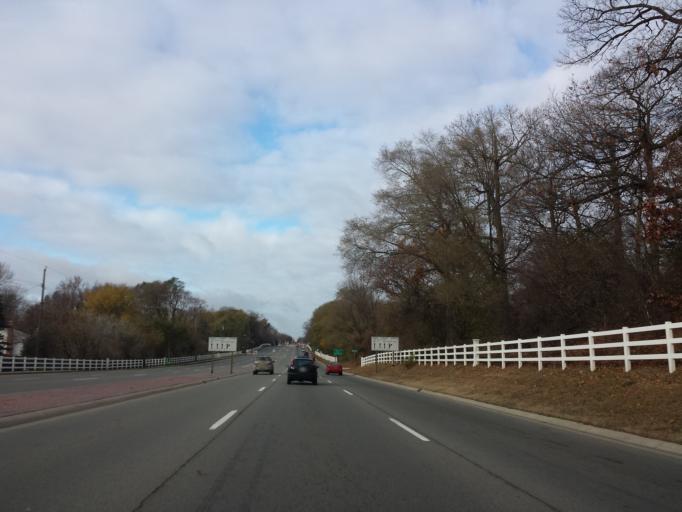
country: US
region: Michigan
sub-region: Oakland County
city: Pontiac
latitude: 42.6033
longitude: -83.2789
